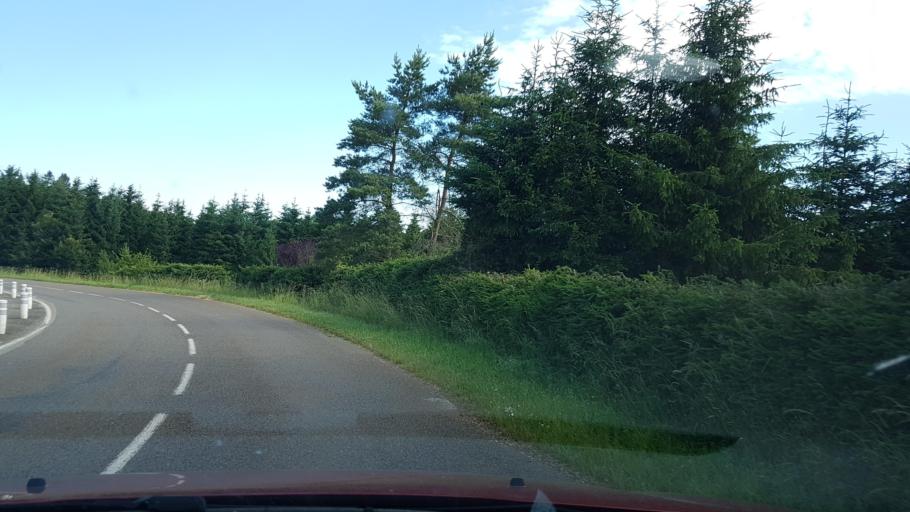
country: FR
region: Franche-Comte
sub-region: Departement du Jura
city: Clairvaux-les-Lacs
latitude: 46.5929
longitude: 5.7318
